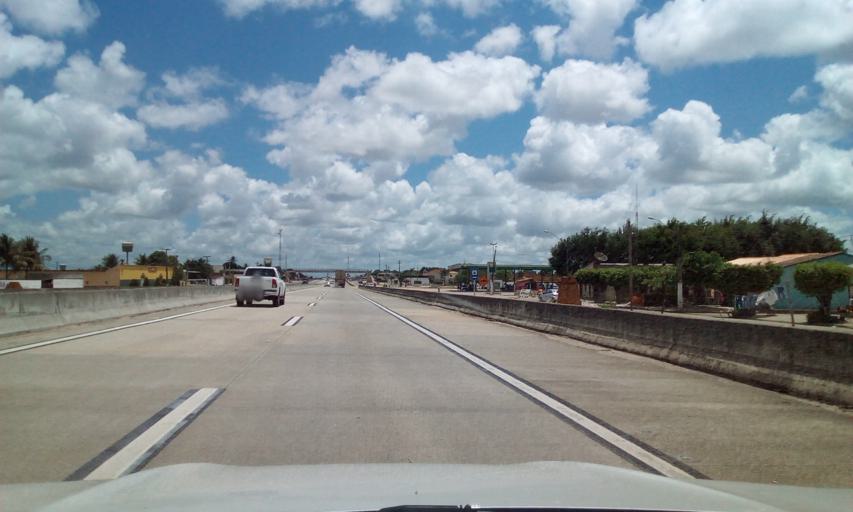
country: BR
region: Alagoas
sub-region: Junqueiro
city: Junqueiro
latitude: -9.9015
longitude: -36.3611
